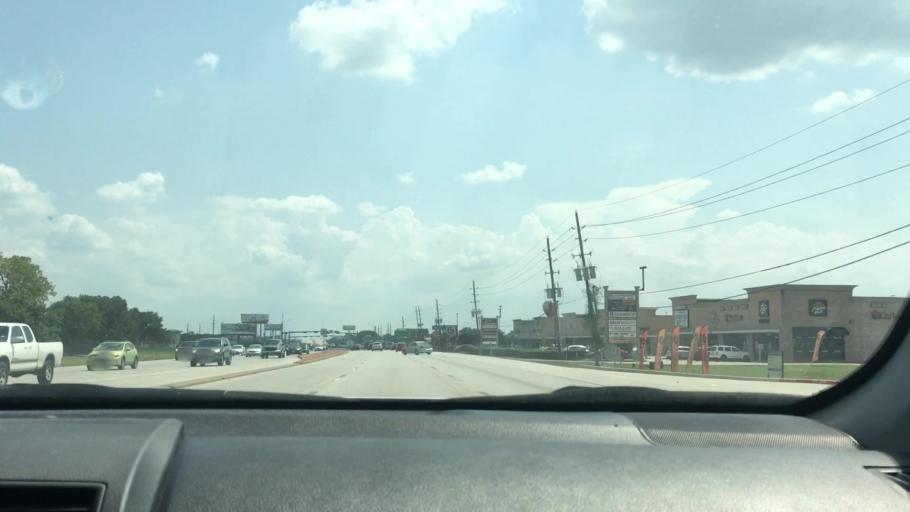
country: US
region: Texas
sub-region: Fort Bend County
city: Mission Bend
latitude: 29.7232
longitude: -95.6442
